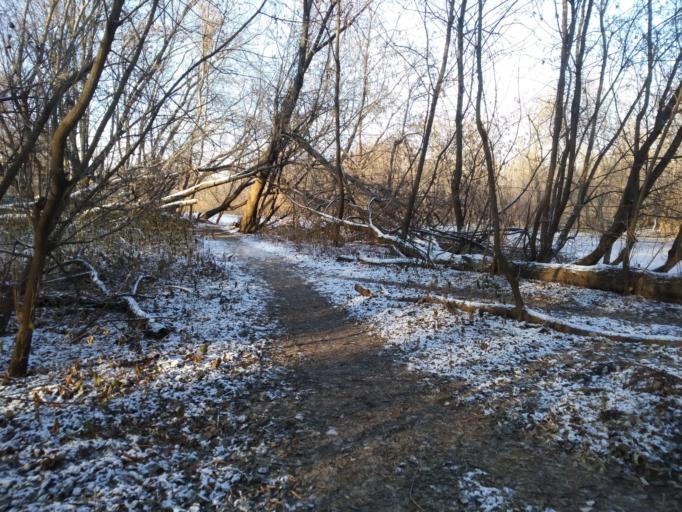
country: RU
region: Kirov
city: Vyatskiye Polyany
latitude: 56.2380
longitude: 51.0762
